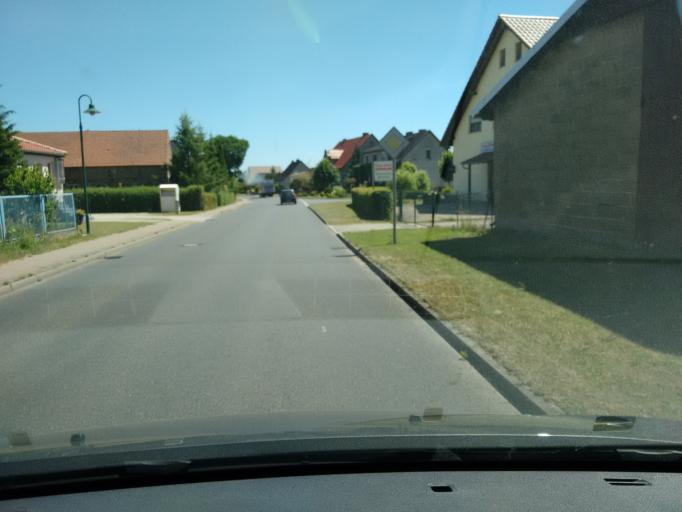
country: DE
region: Brandenburg
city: Rietz Neuendorf
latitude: 52.2125
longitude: 14.2066
